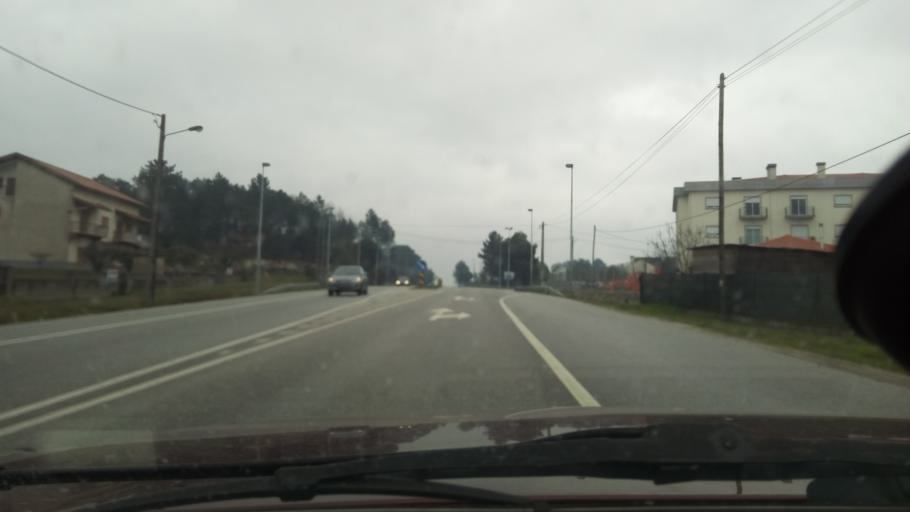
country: PT
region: Viseu
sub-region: Mangualde
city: Mangualde
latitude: 40.6043
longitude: -7.7840
